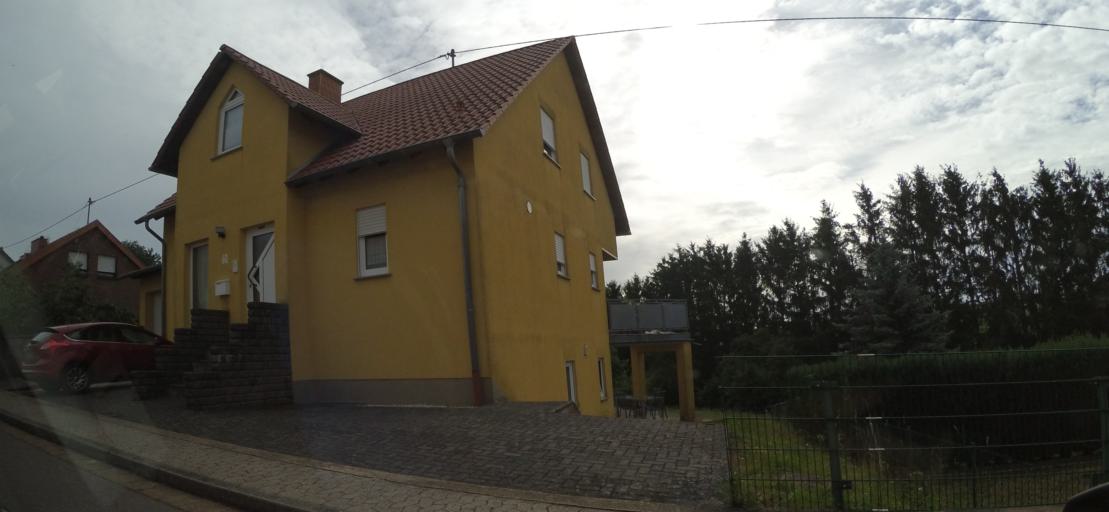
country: DE
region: Saarland
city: Puttlingen
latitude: 49.3107
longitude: 6.9016
